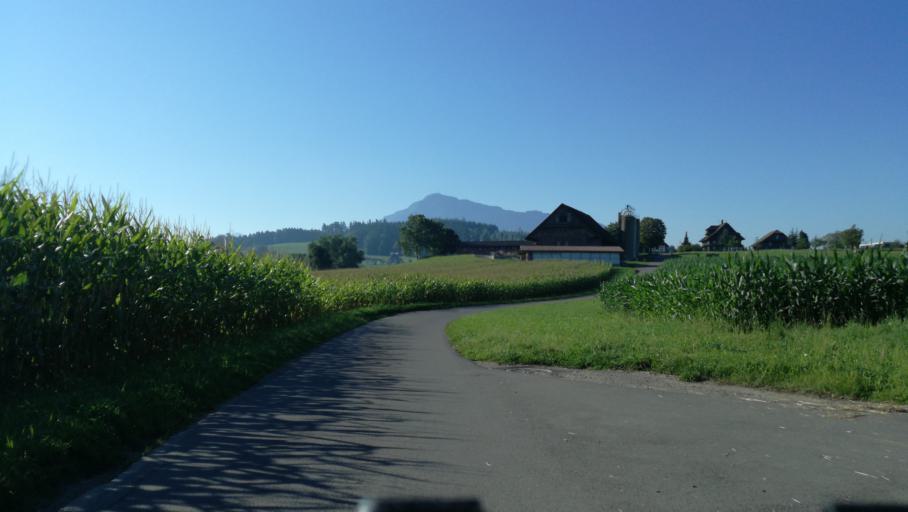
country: CH
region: Lucerne
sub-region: Lucerne-Land District
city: Meierskappel
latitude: 47.1467
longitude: 8.4559
